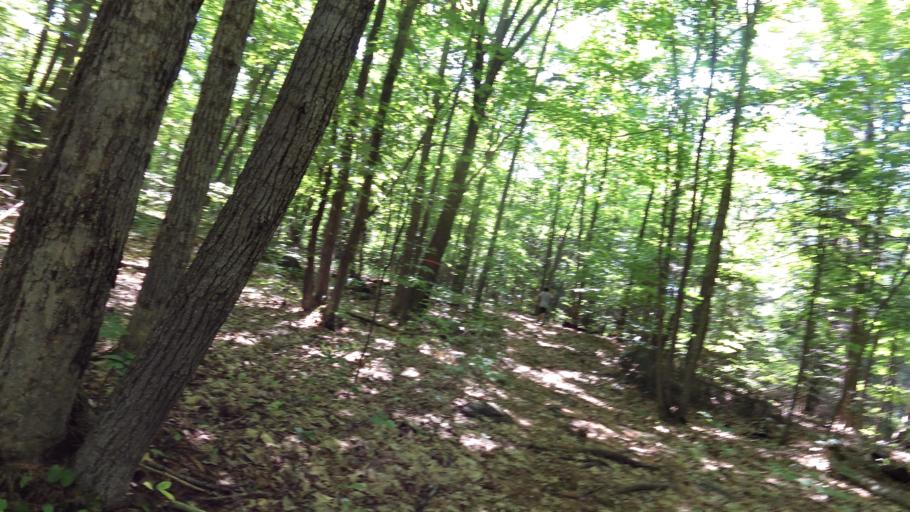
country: CA
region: Ontario
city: Arnprior
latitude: 45.4625
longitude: -76.2648
